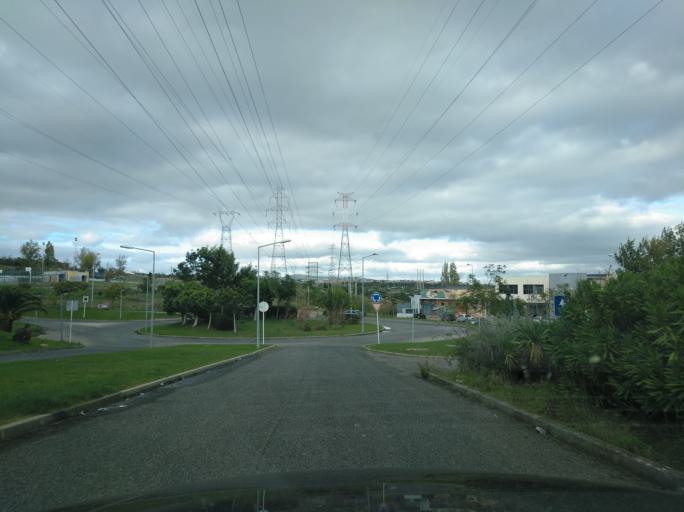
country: PT
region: Lisbon
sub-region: Loures
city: Sacavem
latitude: 38.7999
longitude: -9.1147
